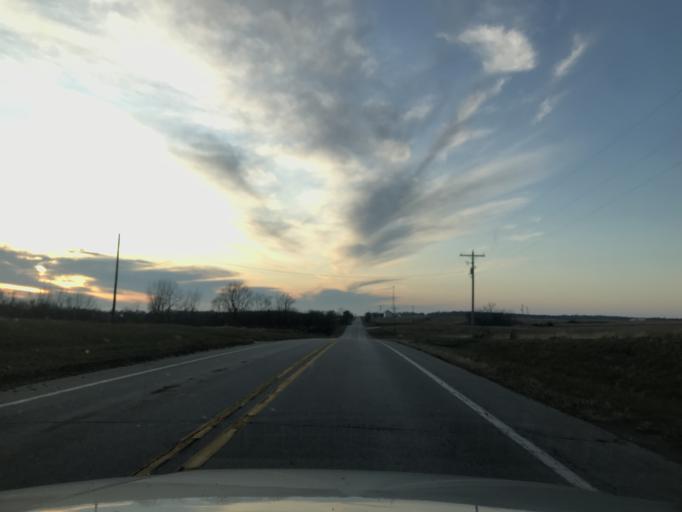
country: US
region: Illinois
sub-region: Henderson County
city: Oquawka
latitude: 41.0189
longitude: -90.8312
